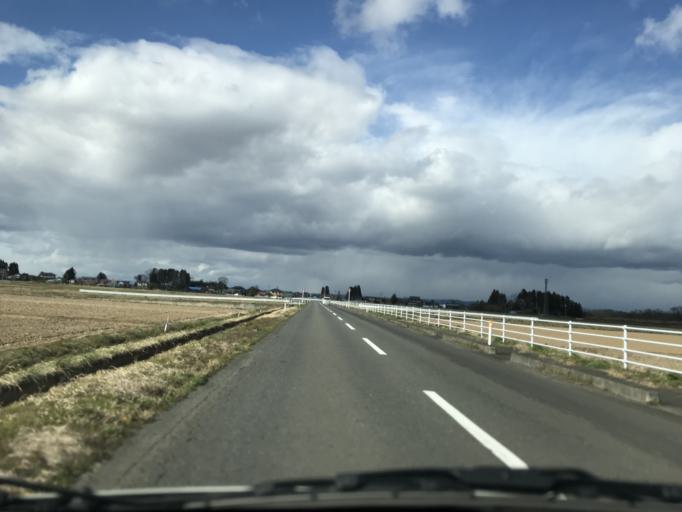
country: JP
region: Miyagi
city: Wakuya
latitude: 38.6518
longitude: 141.2039
